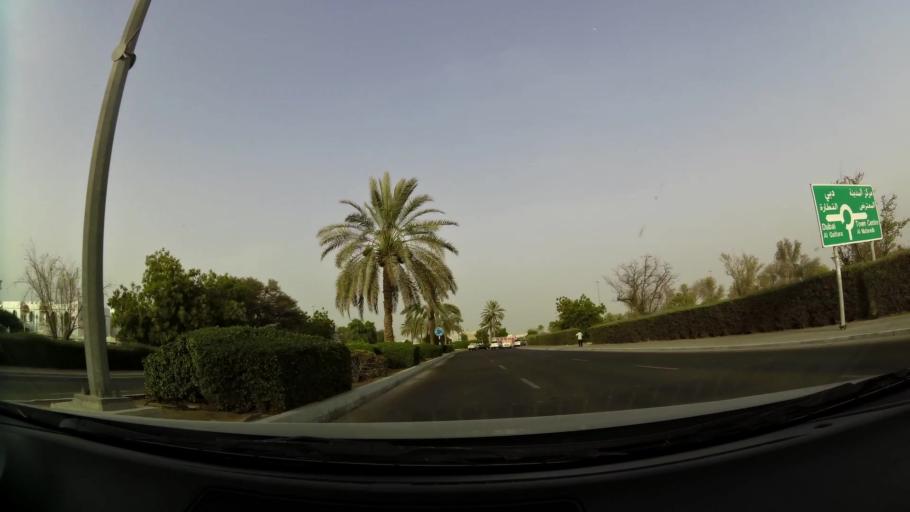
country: OM
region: Al Buraimi
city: Al Buraymi
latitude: 24.2409
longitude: 55.7506
